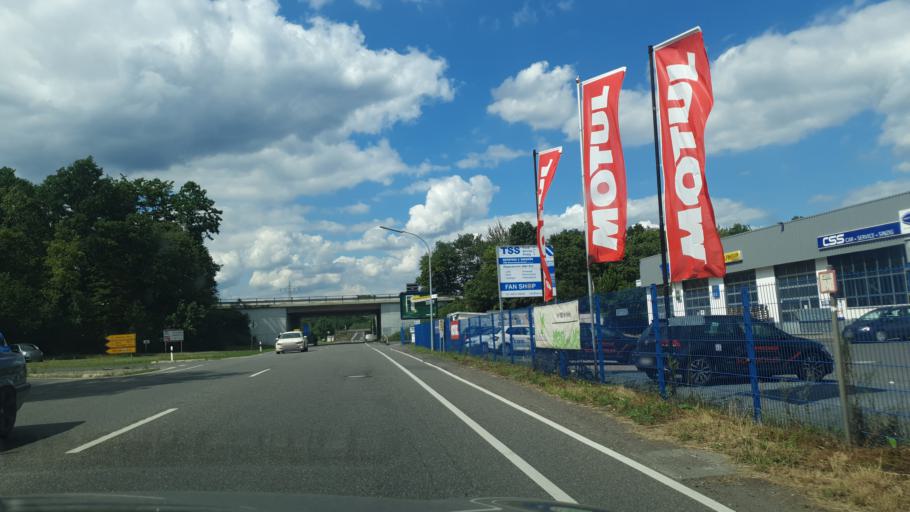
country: DE
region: Rheinland-Pfalz
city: Sinzig
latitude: 50.5544
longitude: 7.2441
